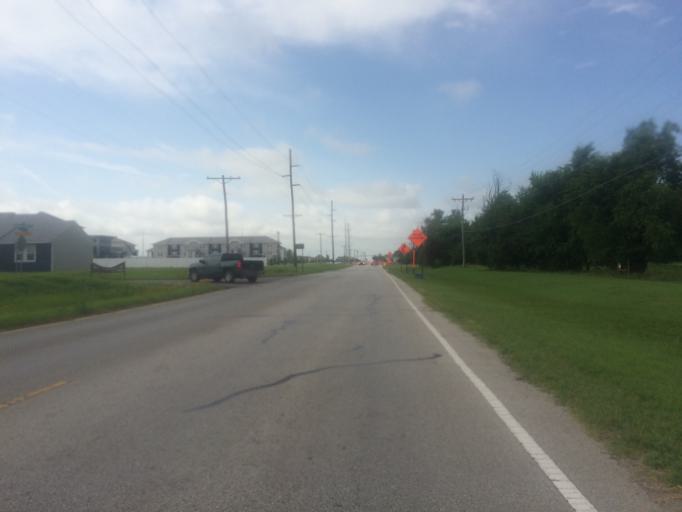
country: US
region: Oklahoma
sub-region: Cleveland County
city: Norman
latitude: 35.1797
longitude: -97.4237
